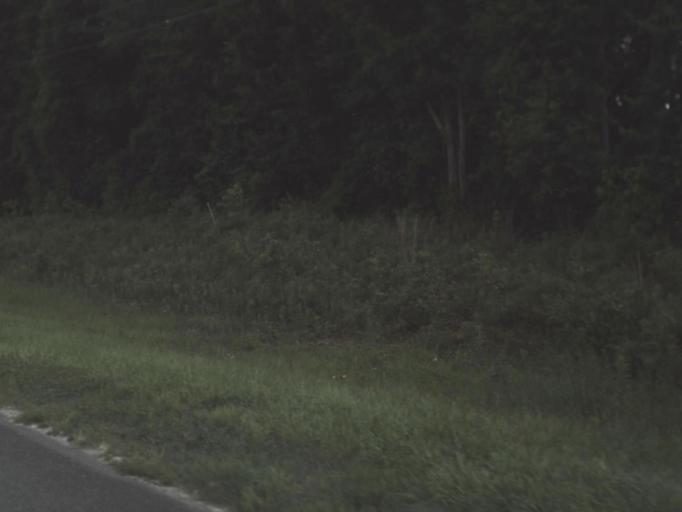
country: US
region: Florida
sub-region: Alachua County
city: High Springs
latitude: 29.8918
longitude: -82.6761
